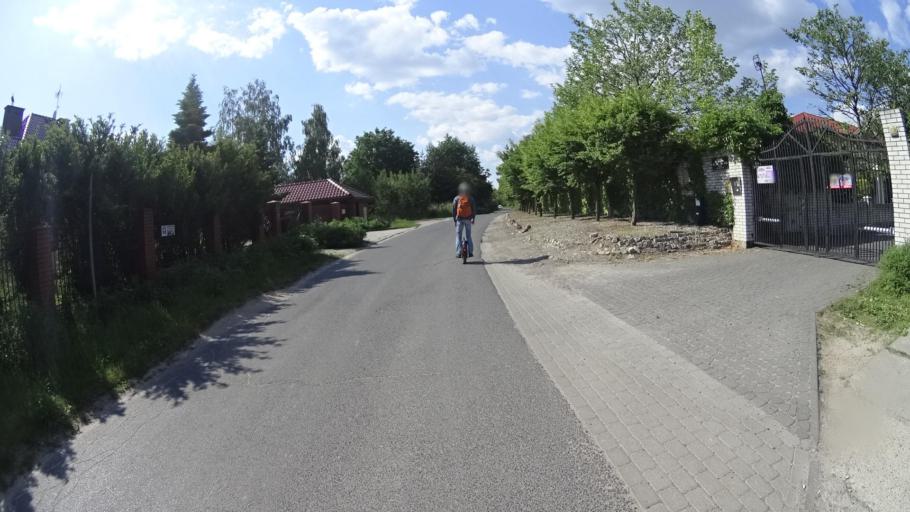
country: PL
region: Masovian Voivodeship
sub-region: Powiat piaseczynski
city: Jozefoslaw
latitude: 52.1070
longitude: 21.0501
